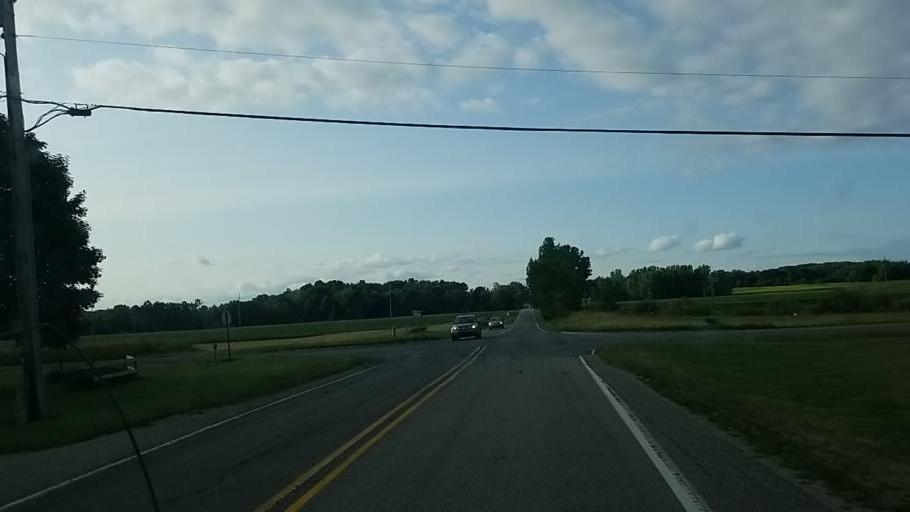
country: US
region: Michigan
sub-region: Montcalm County
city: Greenville
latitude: 43.1089
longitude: -85.3526
